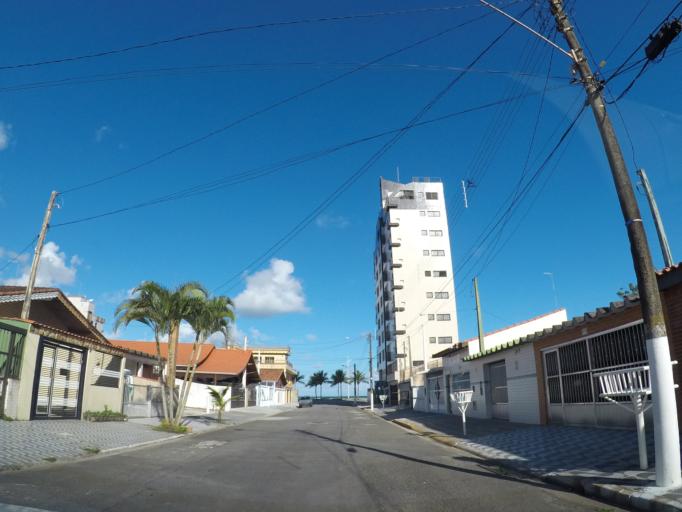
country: BR
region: Sao Paulo
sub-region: Mongagua
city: Mongagua
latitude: -24.0595
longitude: -46.5458
